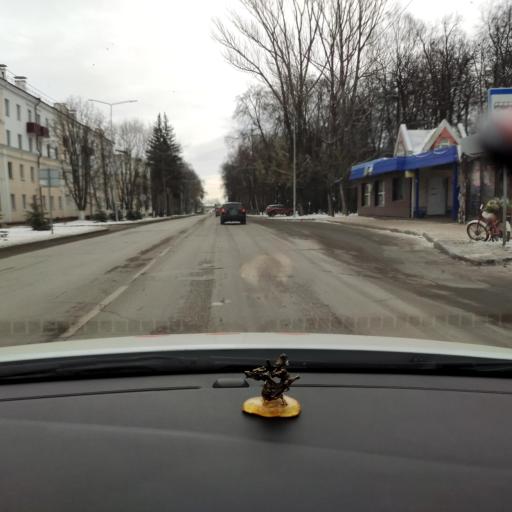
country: RU
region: Tatarstan
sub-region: Zelenodol'skiy Rayon
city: Zelenodolsk
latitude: 55.8456
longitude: 48.5177
